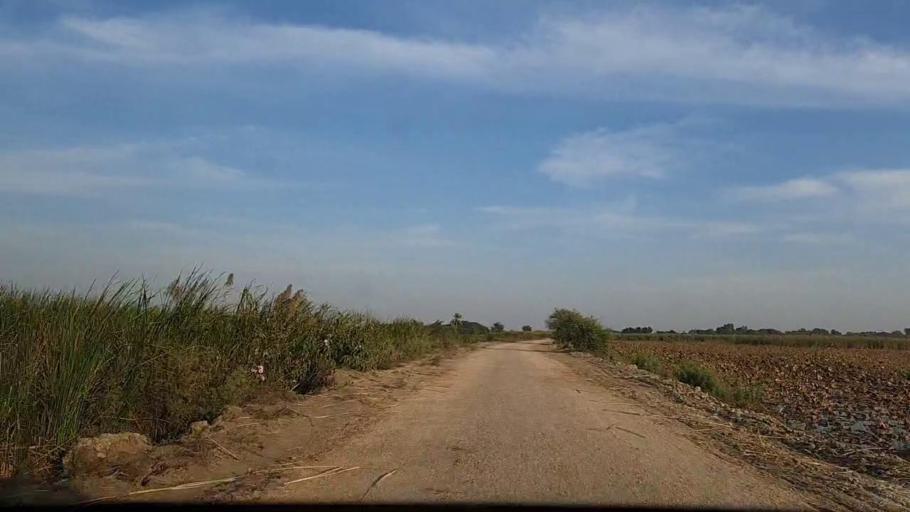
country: PK
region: Sindh
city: Mirpur Batoro
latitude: 24.6573
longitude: 68.1469
